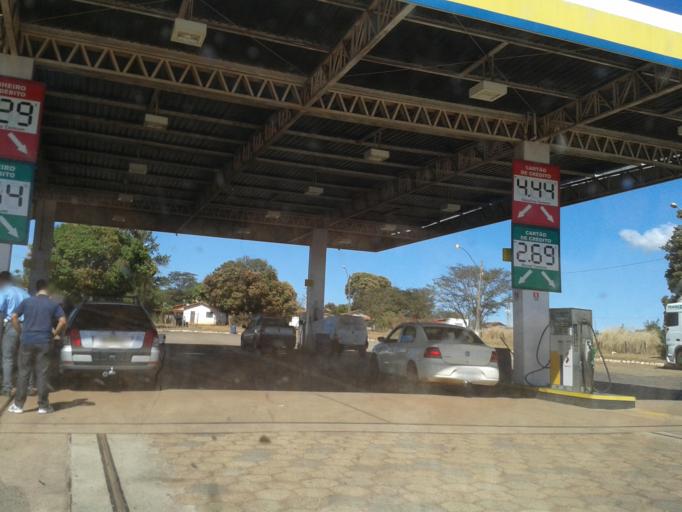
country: BR
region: Goias
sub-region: Pontalina
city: Pontalina
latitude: -17.5275
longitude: -49.2160
